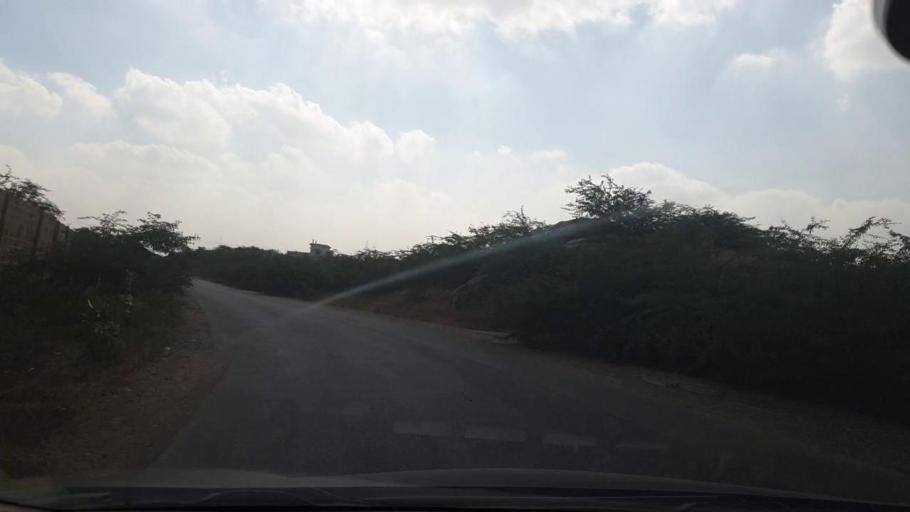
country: PK
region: Sindh
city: Malir Cantonment
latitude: 25.0143
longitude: 67.3525
